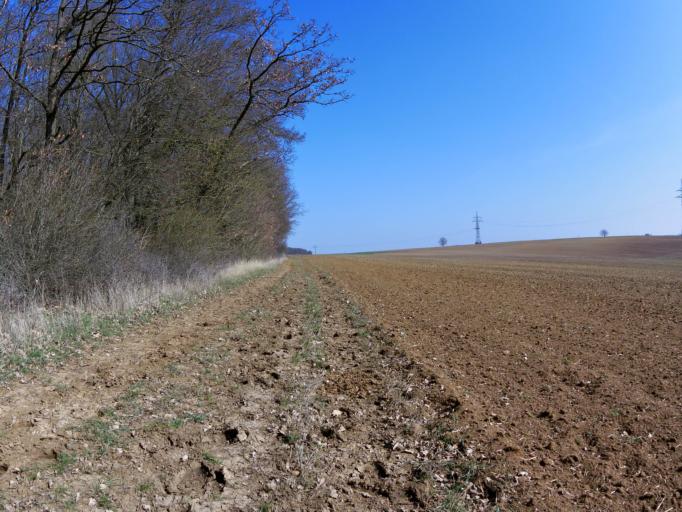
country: DE
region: Bavaria
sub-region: Regierungsbezirk Unterfranken
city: Rottendorf
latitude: 49.8069
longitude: 10.0181
